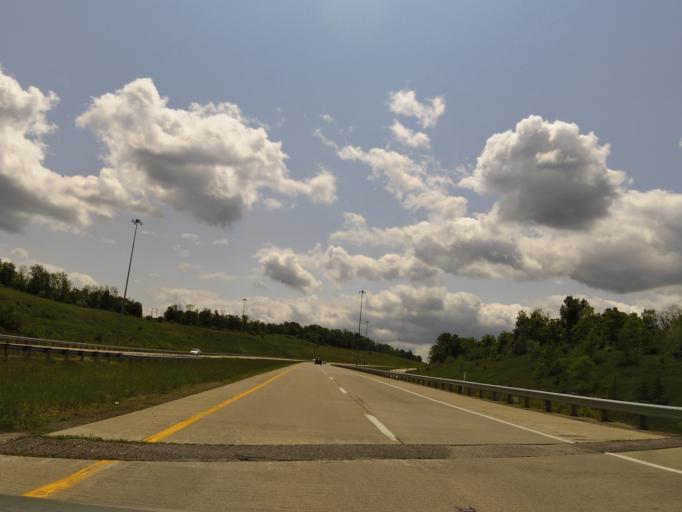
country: US
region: Ohio
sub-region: Athens County
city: Athens
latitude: 39.3031
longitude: -82.1038
